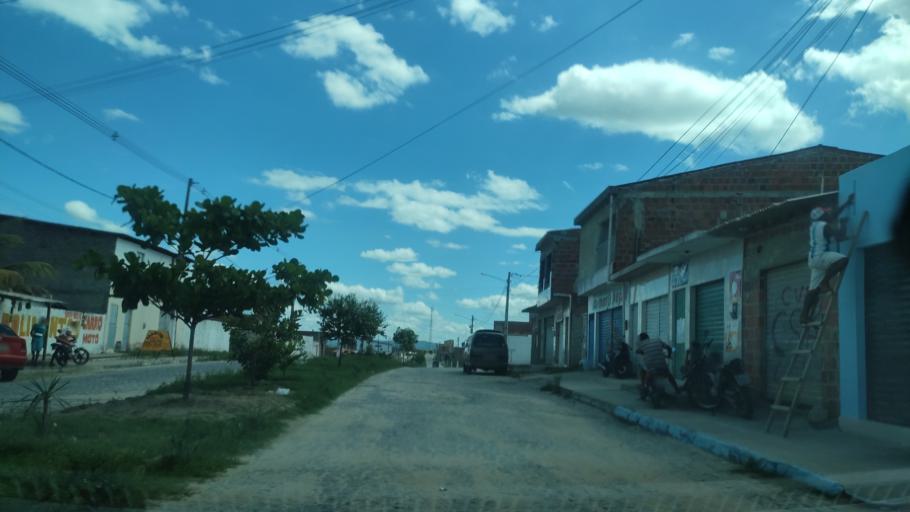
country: BR
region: Alagoas
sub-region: Uniao Dos Palmares
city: Uniao dos Palmares
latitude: -9.1489
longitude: -36.0061
